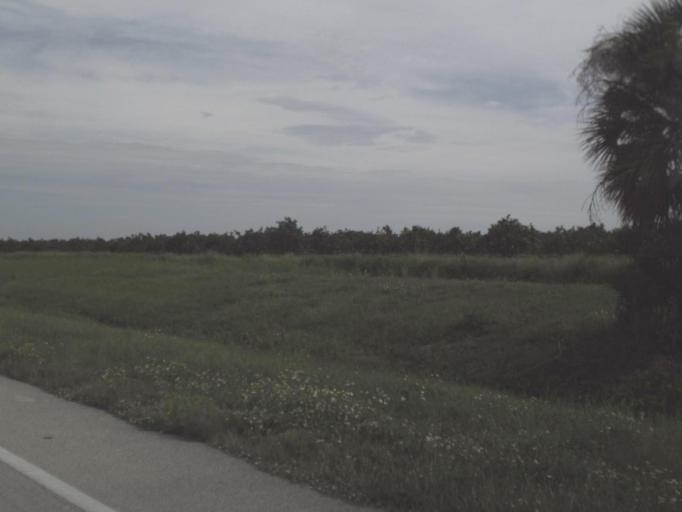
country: US
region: Florida
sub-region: DeSoto County
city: Nocatee
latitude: 27.0829
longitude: -81.7952
